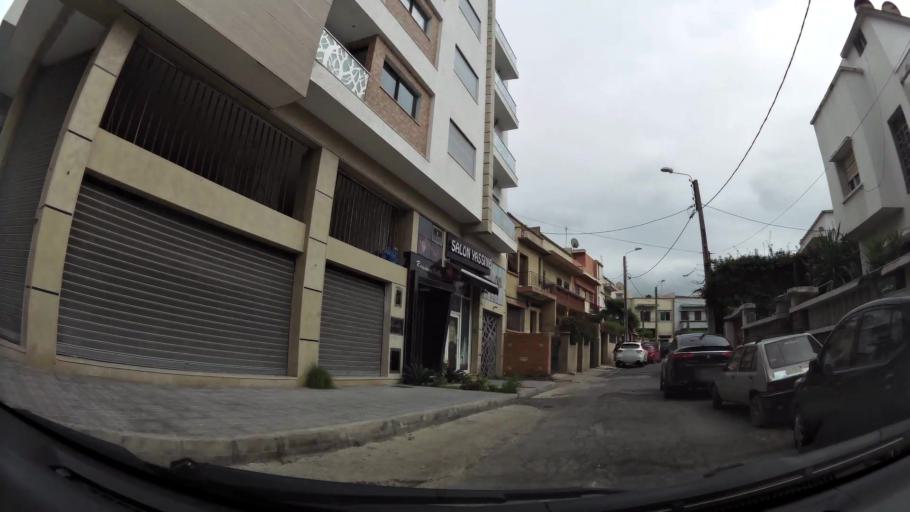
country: MA
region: Grand Casablanca
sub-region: Casablanca
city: Casablanca
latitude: 33.5701
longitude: -7.6097
